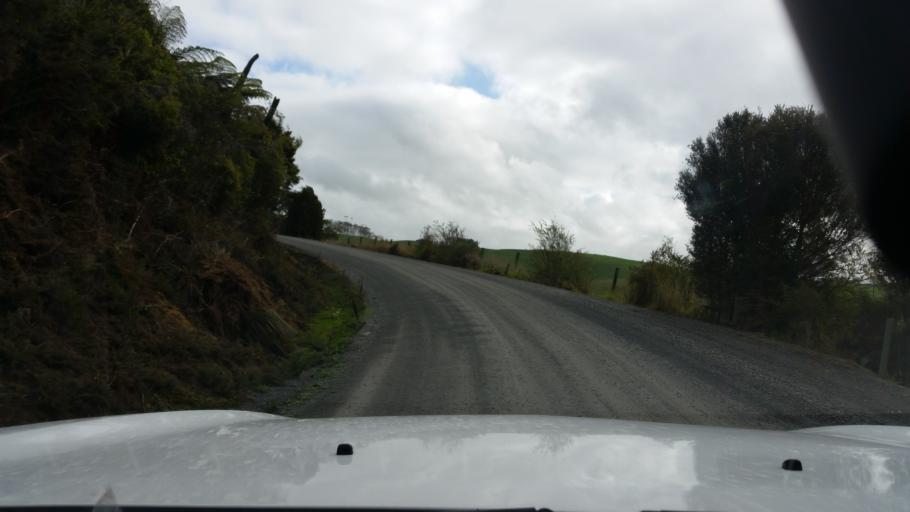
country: NZ
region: Northland
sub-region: Far North District
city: Kawakawa
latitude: -35.5318
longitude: 174.1813
